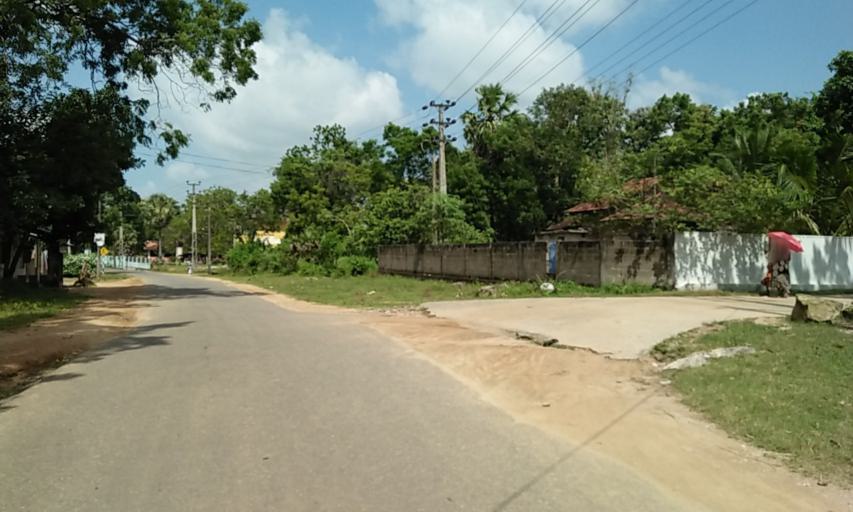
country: LK
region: Eastern Province
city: Ampara
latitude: 7.3360
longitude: 81.7431
